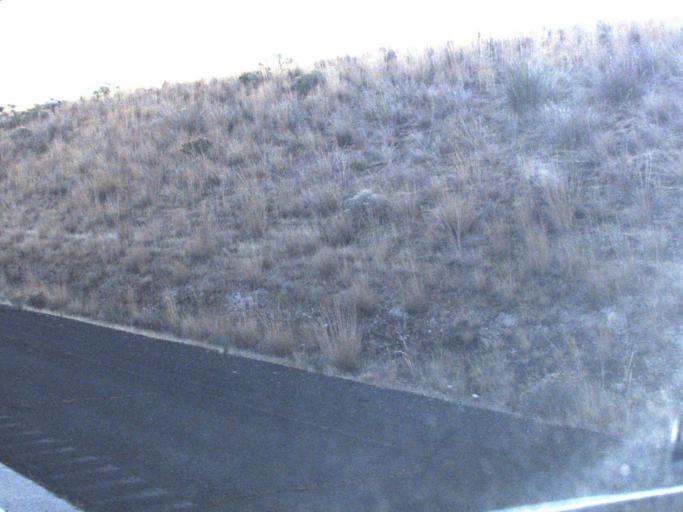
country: US
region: Washington
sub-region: Adams County
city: Ritzville
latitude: 47.0113
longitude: -118.5120
